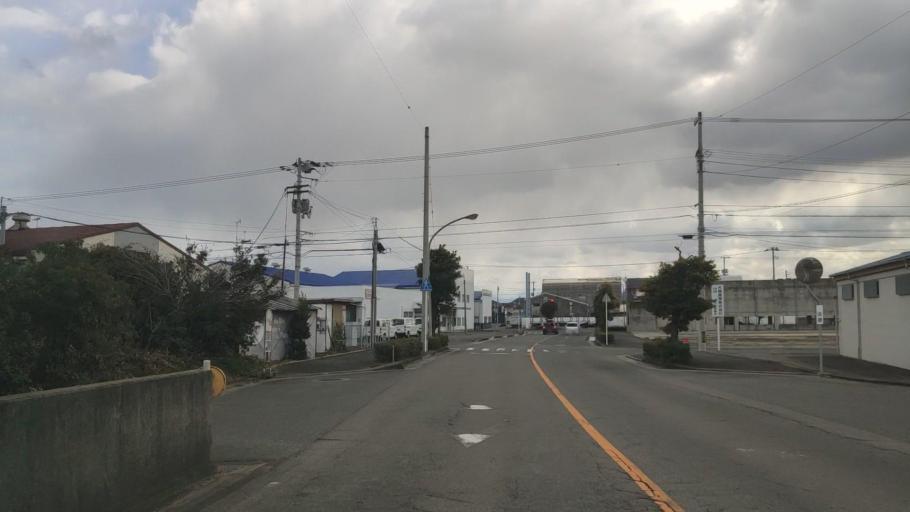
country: JP
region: Ehime
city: Saijo
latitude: 34.0574
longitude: 133.0180
